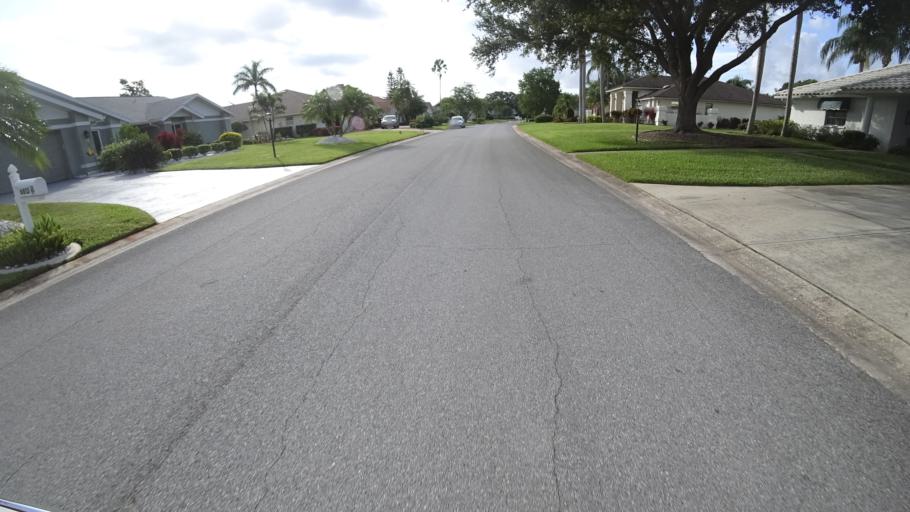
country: US
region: Florida
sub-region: Sarasota County
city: Desoto Lakes
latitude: 27.4195
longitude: -82.4944
